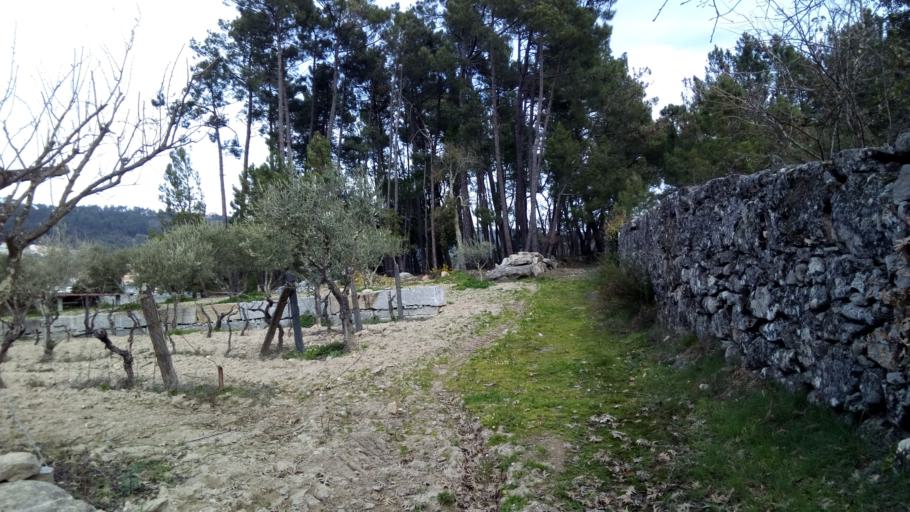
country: PT
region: Guarda
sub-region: Fornos de Algodres
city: Fornos de Algodres
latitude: 40.6148
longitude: -7.5315
